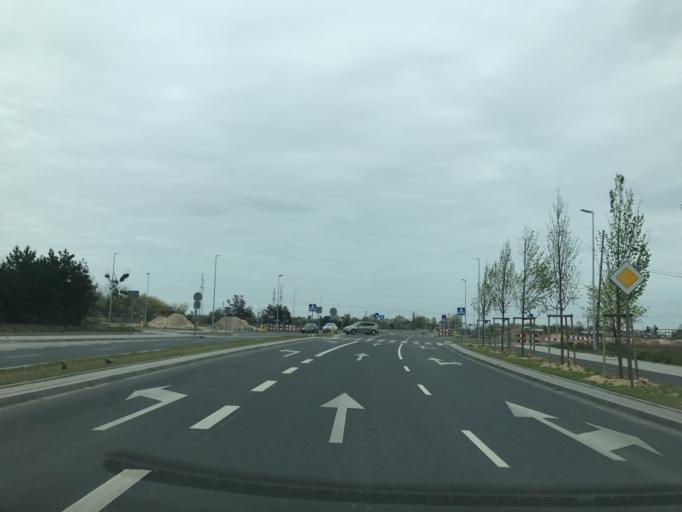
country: PL
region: Kujawsko-Pomorskie
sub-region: Torun
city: Torun
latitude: 53.0417
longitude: 18.6081
